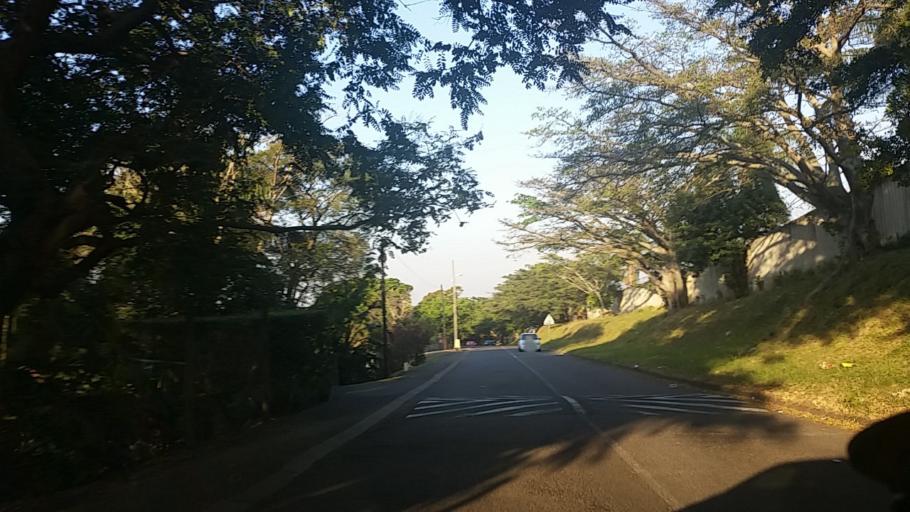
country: ZA
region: KwaZulu-Natal
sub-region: eThekwini Metropolitan Municipality
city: Berea
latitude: -29.8535
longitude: 30.9189
